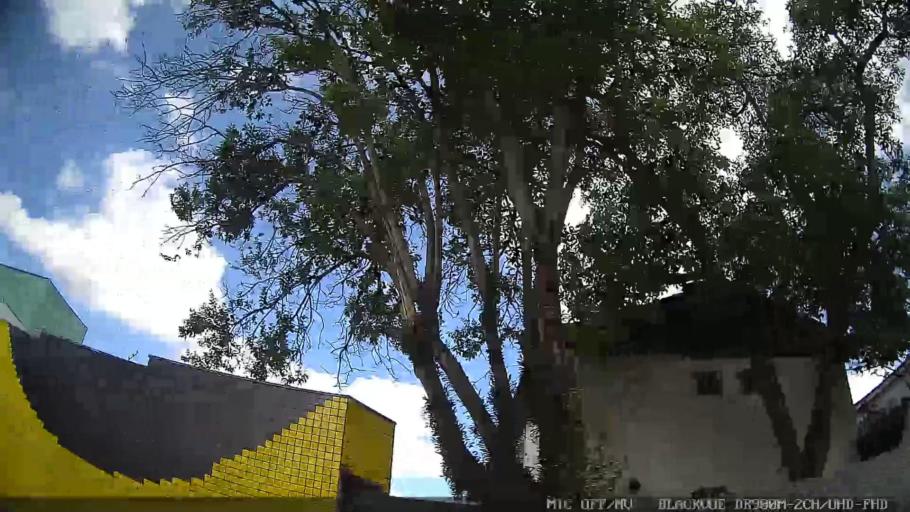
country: BR
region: Sao Paulo
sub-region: Diadema
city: Diadema
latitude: -23.6603
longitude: -46.6046
